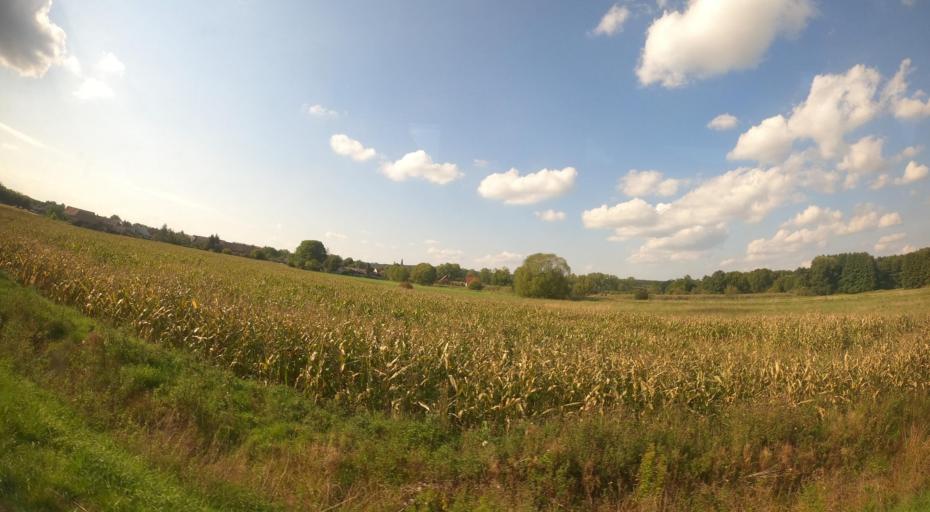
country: PL
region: Lubusz
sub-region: Powiat zielonogorski
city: Swidnica
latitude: 51.8755
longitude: 15.3213
